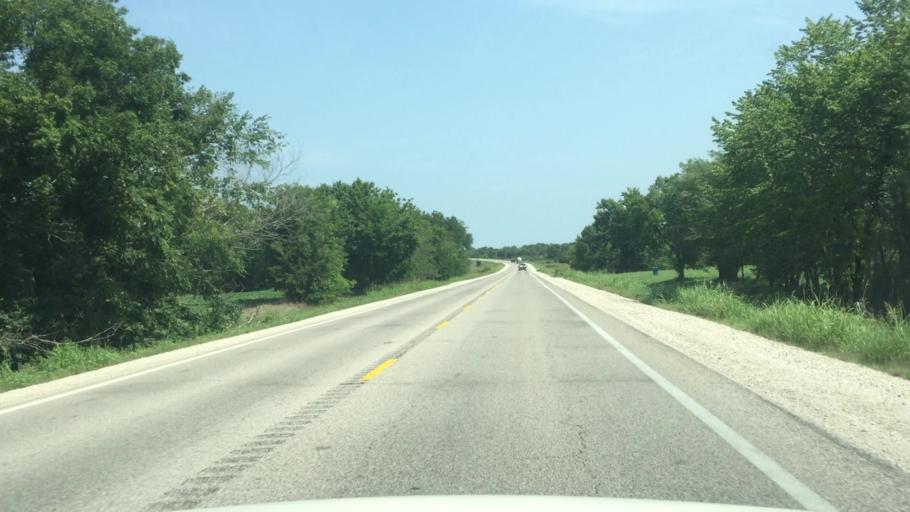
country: US
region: Kansas
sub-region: Montgomery County
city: Coffeyville
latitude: 37.1305
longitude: -95.5790
